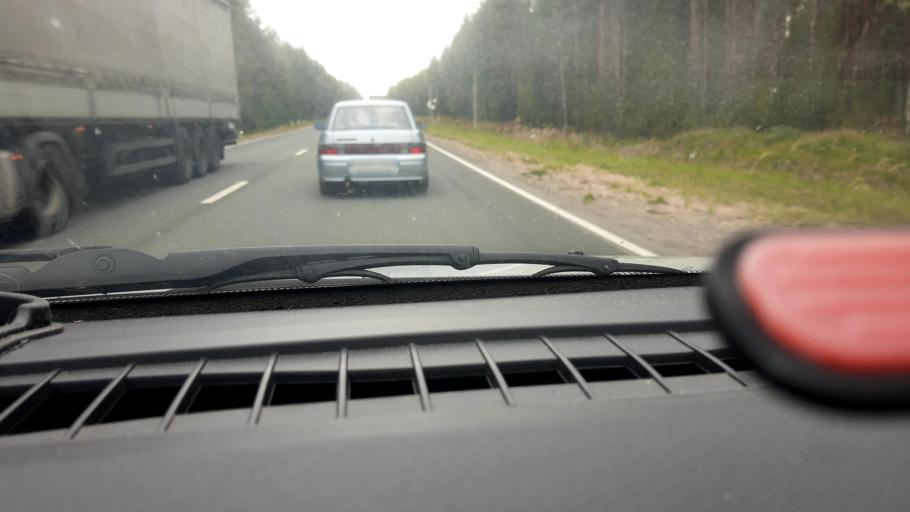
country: RU
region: Nizjnij Novgorod
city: Uren'
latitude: 57.3641
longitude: 45.6964
